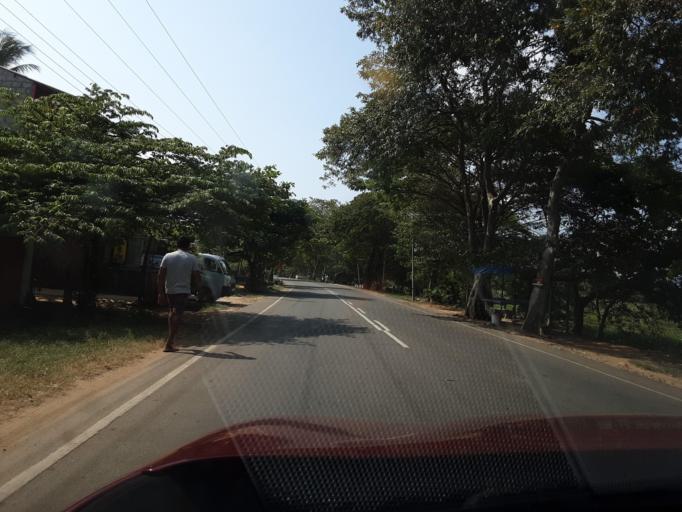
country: LK
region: Southern
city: Tangalla
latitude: 6.3089
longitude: 81.2321
